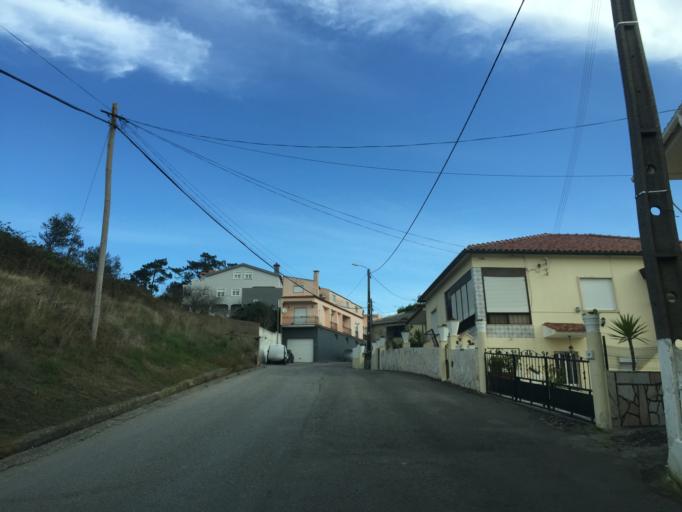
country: PT
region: Lisbon
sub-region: Odivelas
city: Canecas
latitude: 38.8149
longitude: -9.2505
